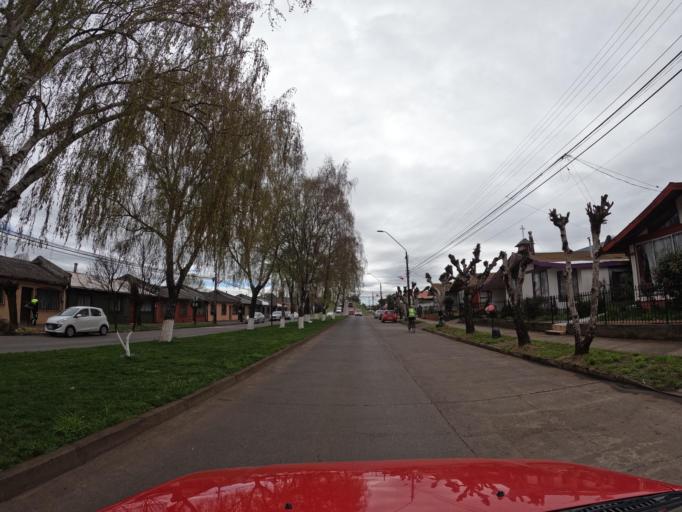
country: CL
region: Araucania
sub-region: Provincia de Malleco
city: Victoria
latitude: -38.2365
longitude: -72.3281
